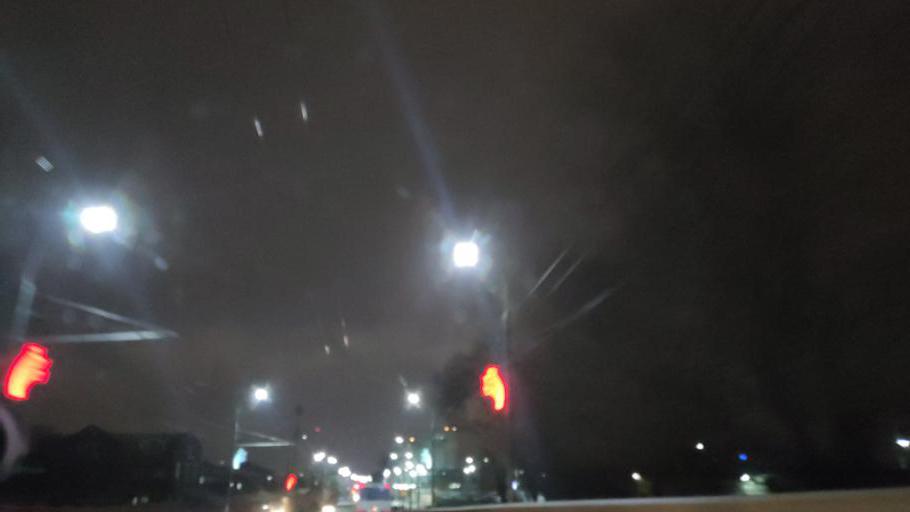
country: RU
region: Moskovskaya
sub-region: Podol'skiy Rayon
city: Podol'sk
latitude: 55.4256
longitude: 37.5610
